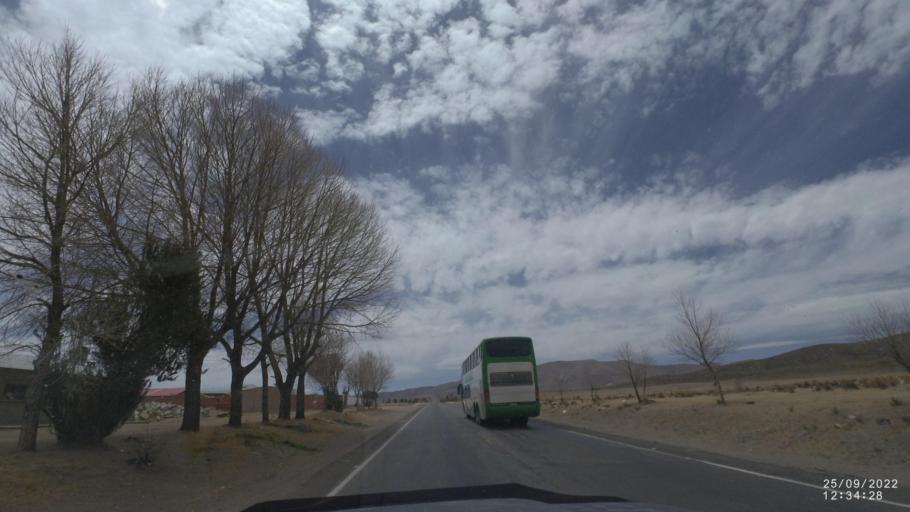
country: BO
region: Oruro
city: Machacamarca
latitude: -18.1749
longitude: -67.0143
